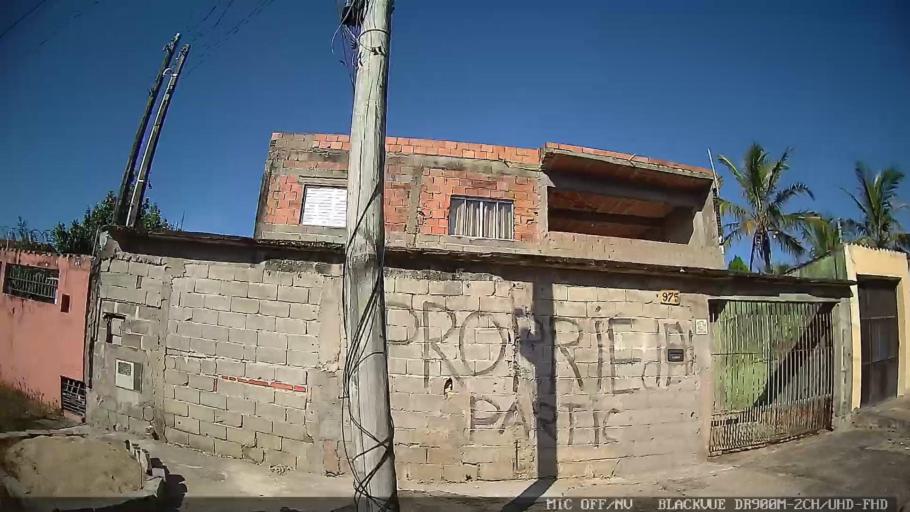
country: BR
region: Sao Paulo
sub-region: Peruibe
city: Peruibe
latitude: -24.2764
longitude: -46.9525
